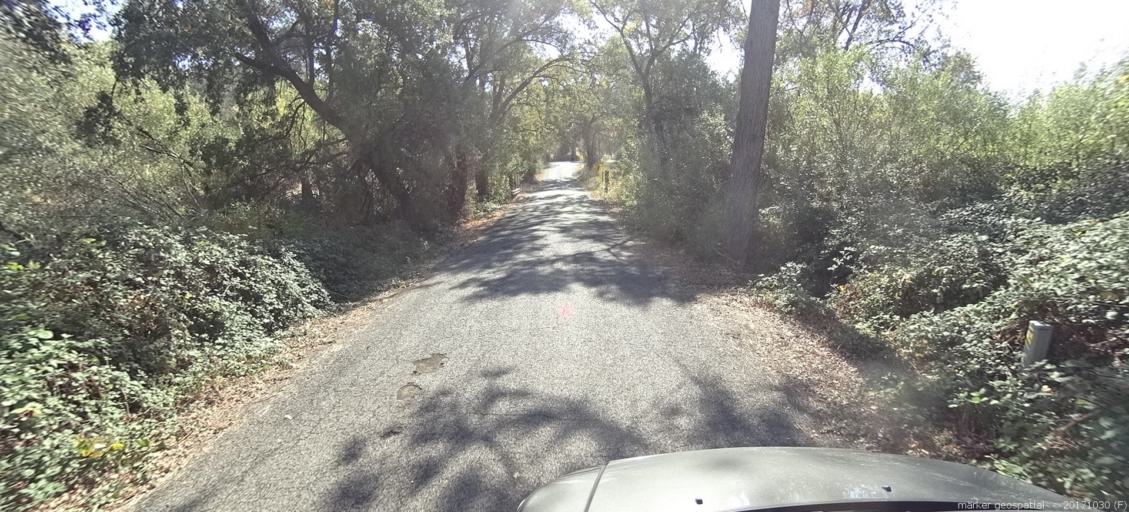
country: US
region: California
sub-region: Shasta County
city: Shingletown
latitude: 40.5147
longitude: -121.9741
